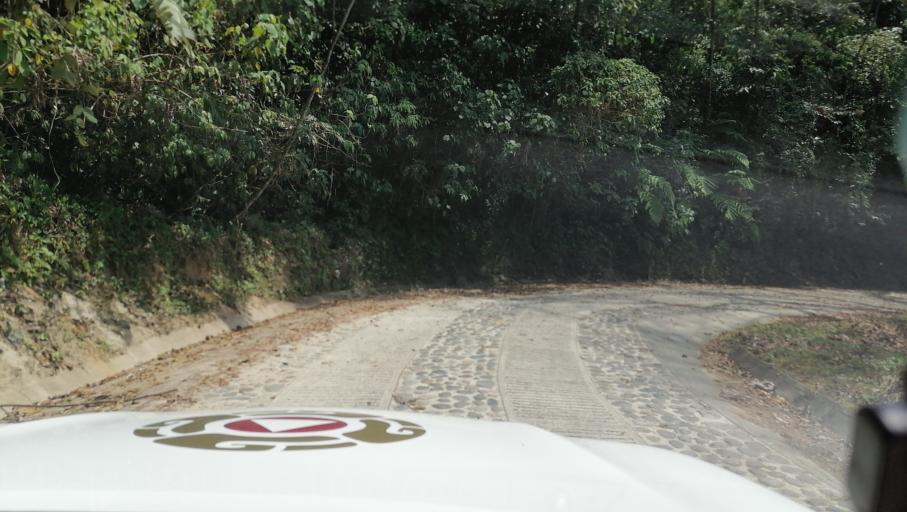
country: MX
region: Chiapas
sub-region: Tapachula
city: Canton Villaflor
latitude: 15.1350
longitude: -92.2920
